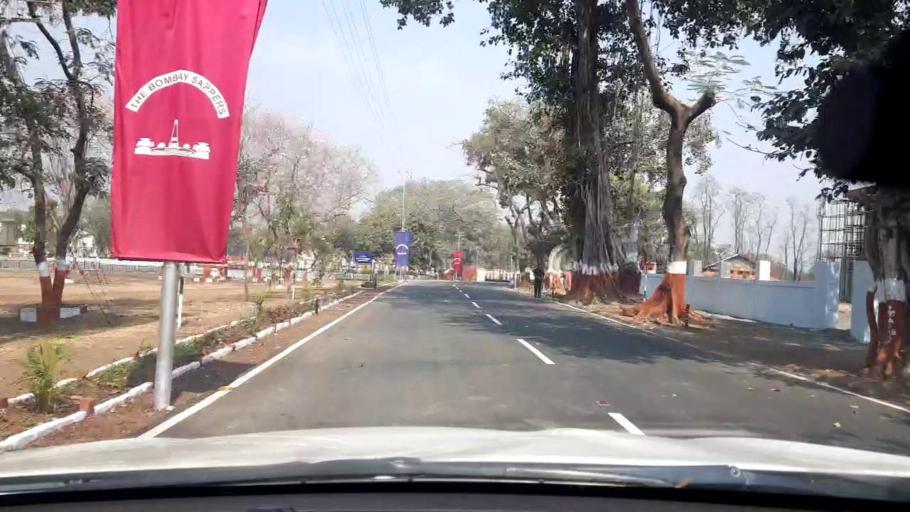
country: IN
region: Maharashtra
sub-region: Pune Division
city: Khadki
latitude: 18.5494
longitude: 73.8670
